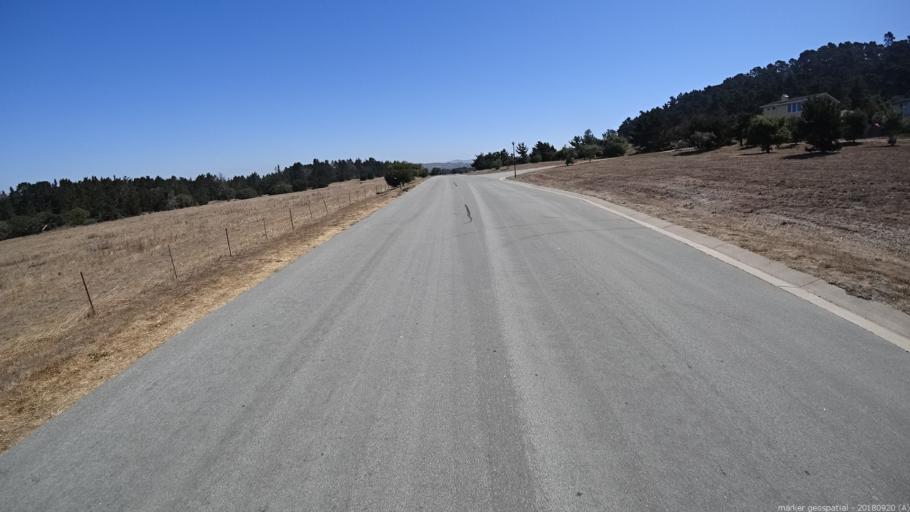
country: US
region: California
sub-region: Monterey County
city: Del Rey Oaks
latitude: 36.5791
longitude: -121.8482
